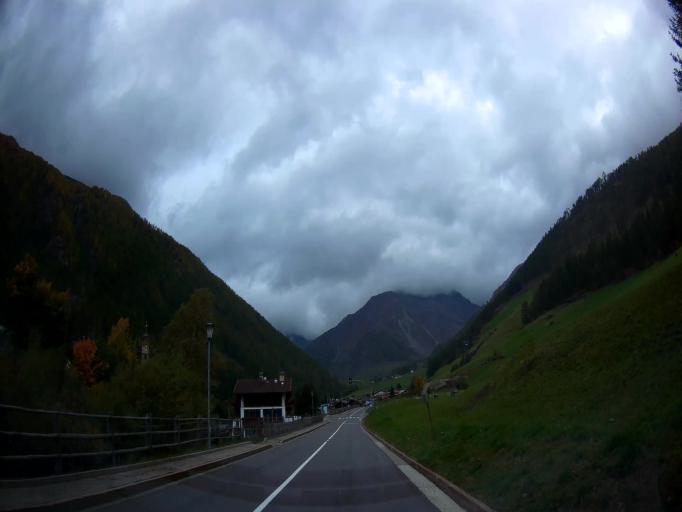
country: IT
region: Trentino-Alto Adige
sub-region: Bolzano
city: Senales
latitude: 46.7218
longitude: 10.8619
